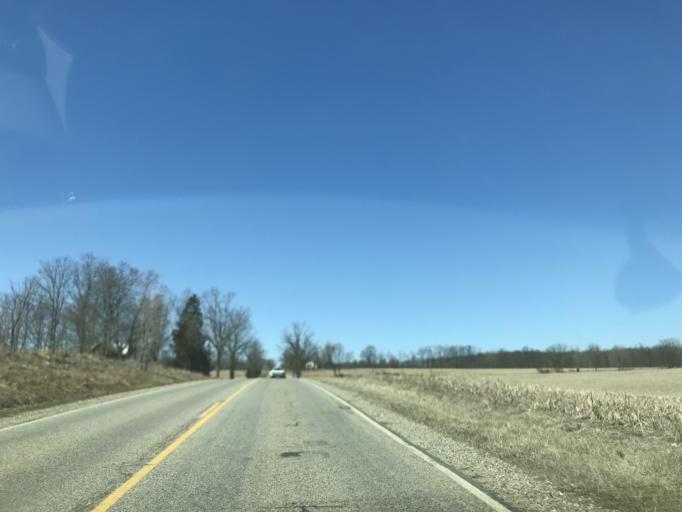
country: US
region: Michigan
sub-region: Hillsdale County
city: Litchfield
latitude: 41.9857
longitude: -84.7771
